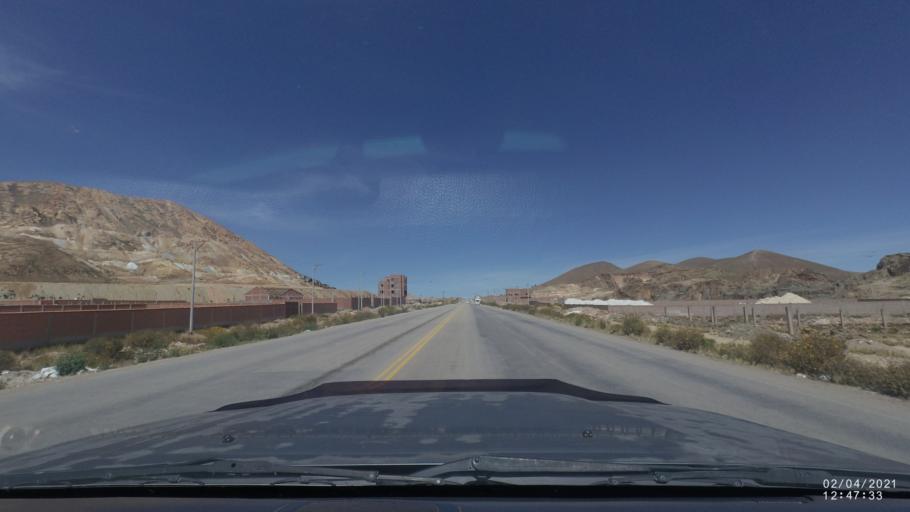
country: BO
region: Oruro
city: Oruro
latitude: -17.9541
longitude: -67.1437
